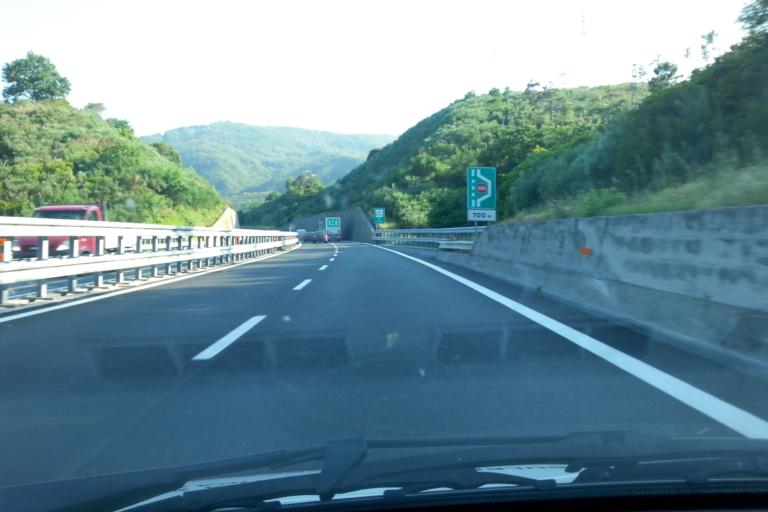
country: IT
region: Liguria
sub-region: Provincia di Savona
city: Valle di Vado
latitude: 44.2613
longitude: 8.4077
